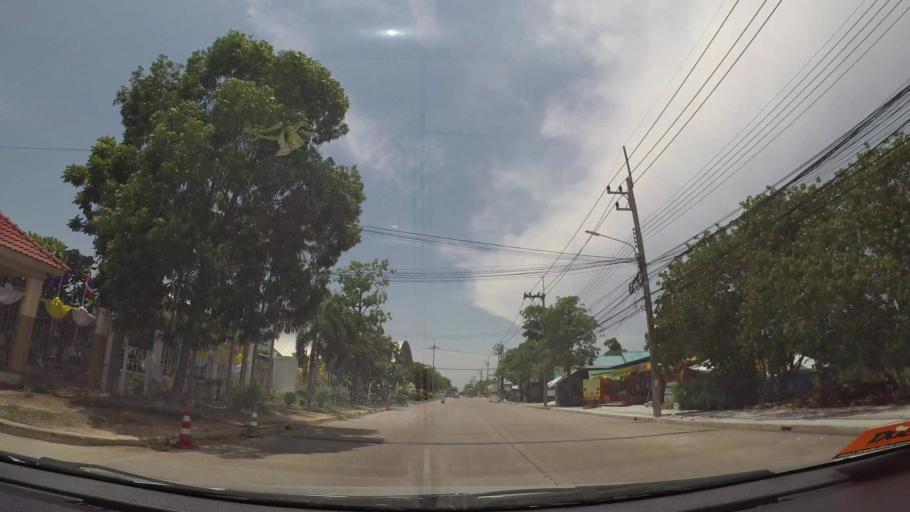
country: TH
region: Chon Buri
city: Chon Buri
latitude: 13.3418
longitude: 100.9448
